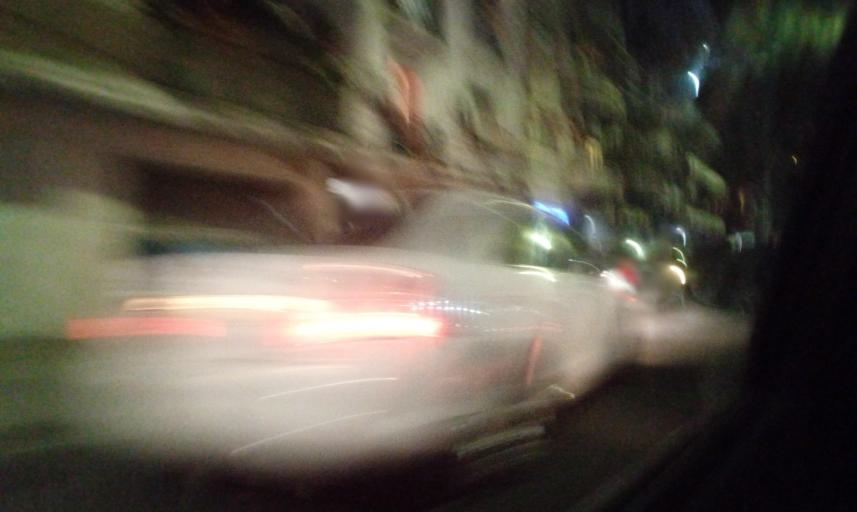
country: AR
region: Buenos Aires F.D.
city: Villa Santa Rita
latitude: -34.6198
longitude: -58.4372
